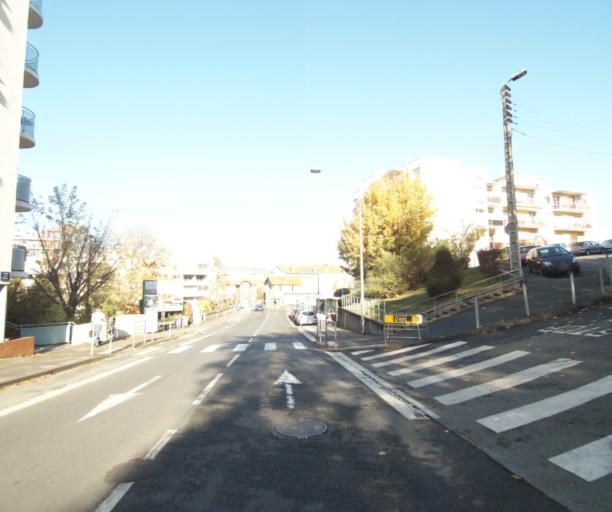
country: FR
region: Auvergne
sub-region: Departement du Puy-de-Dome
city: Clermont-Ferrand
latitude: 45.7708
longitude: 3.0945
